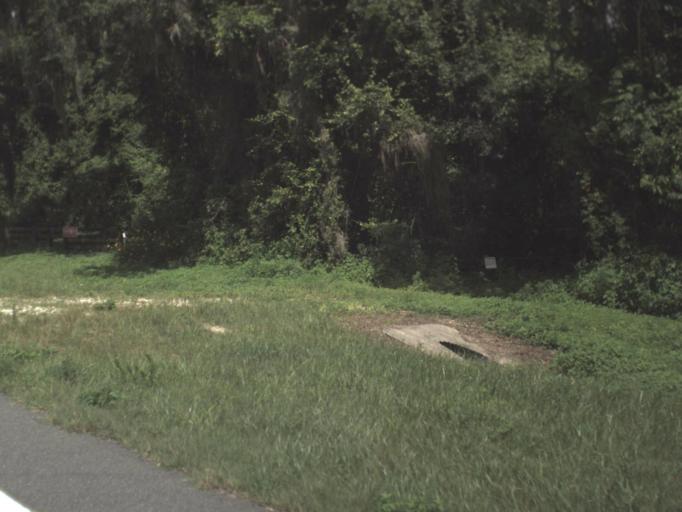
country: US
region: Florida
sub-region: Alachua County
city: Alachua
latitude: 29.8169
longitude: -82.4530
